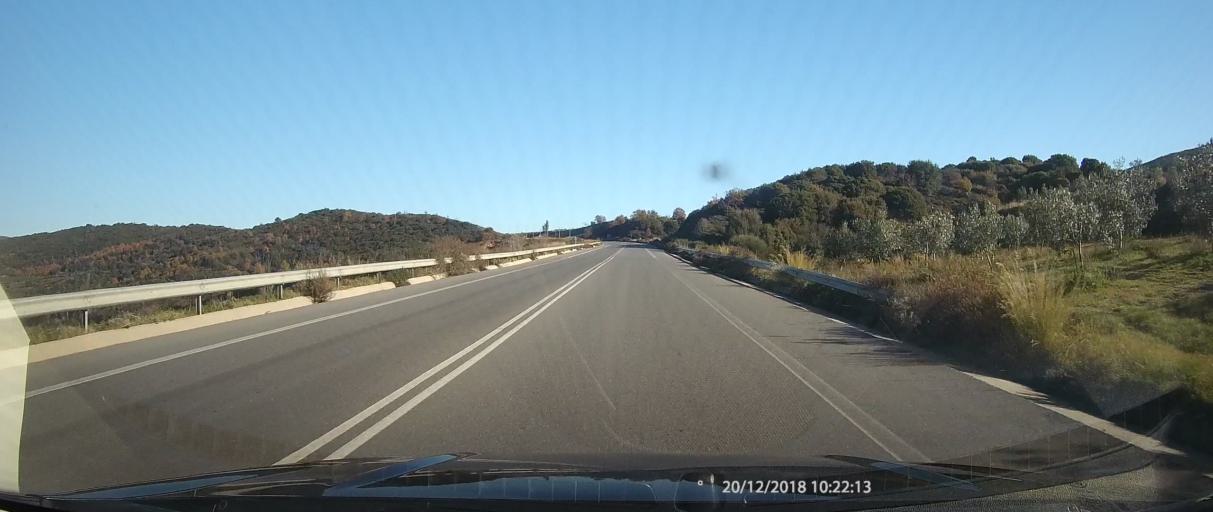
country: GR
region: Peloponnese
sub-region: Nomos Lakonias
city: Magoula
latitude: 37.1712
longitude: 22.4272
